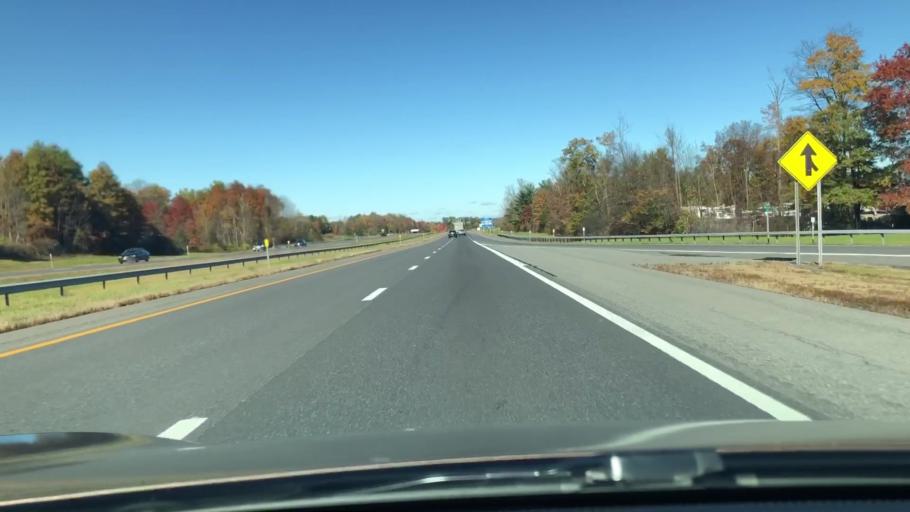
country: US
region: New York
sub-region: Ulster County
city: Saugerties South
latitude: 42.0560
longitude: -73.9832
